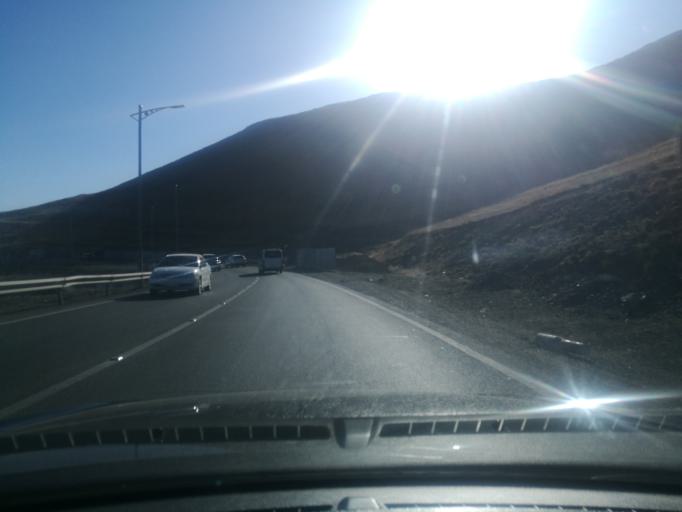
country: MN
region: Ulaanbaatar
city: Ulaanbaatar
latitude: 47.8862
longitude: 106.8694
